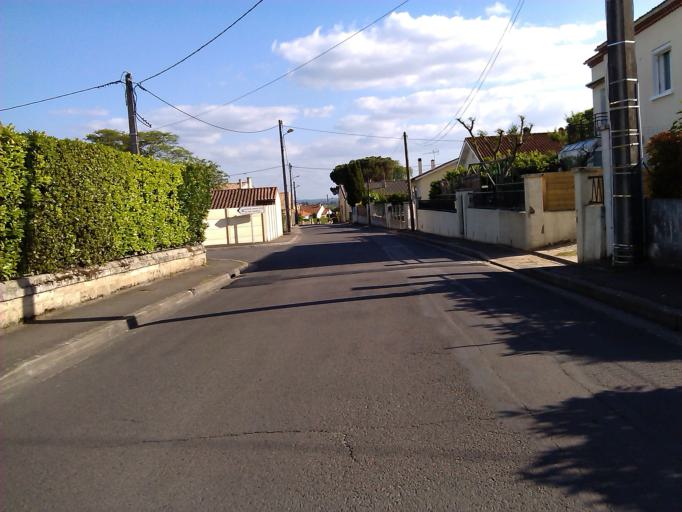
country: FR
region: Aquitaine
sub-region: Departement de la Gironde
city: Saint-Gervais
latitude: 44.9974
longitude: -0.4484
